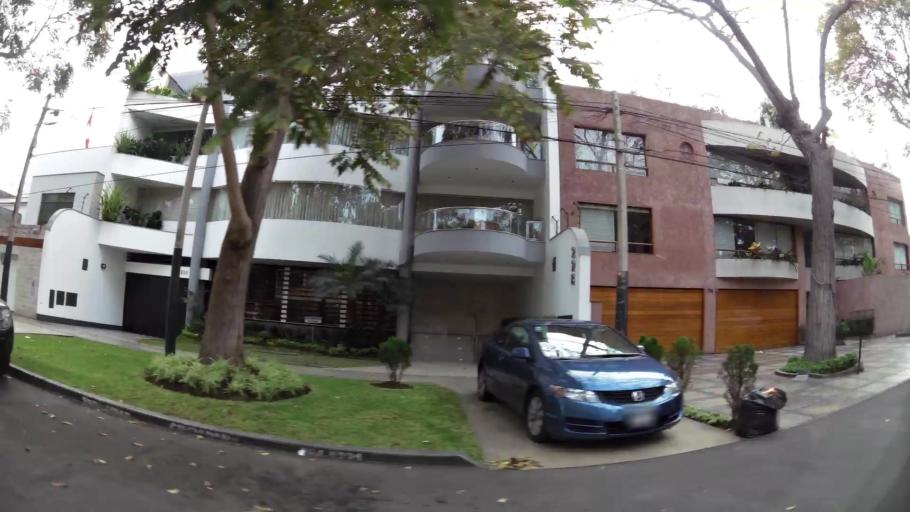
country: PE
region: Lima
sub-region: Lima
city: San Isidro
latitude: -12.1069
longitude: -77.0435
